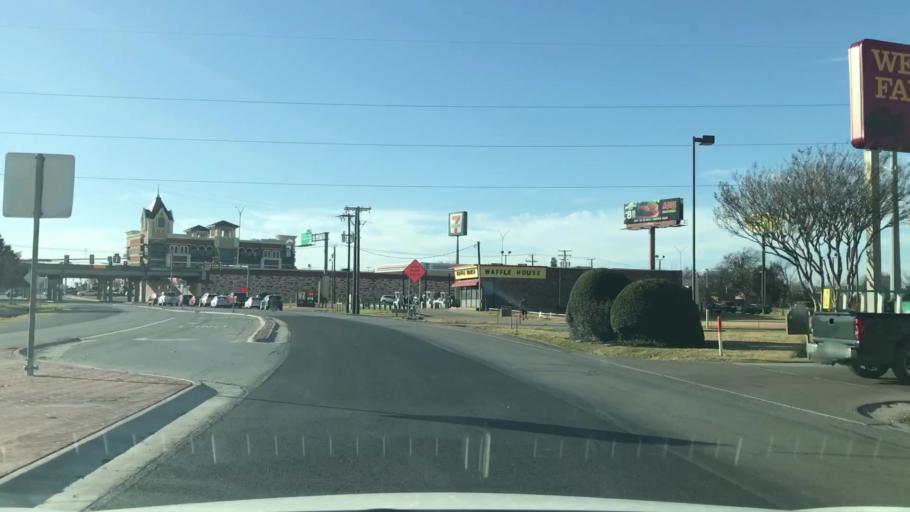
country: US
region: Texas
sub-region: Johnson County
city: Burleson
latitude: 32.5441
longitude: -97.3128
